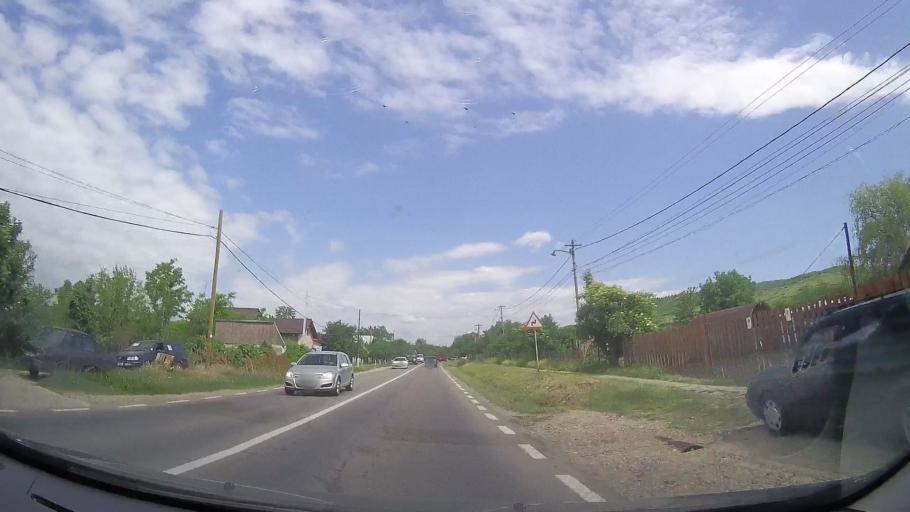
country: RO
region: Prahova
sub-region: Comuna Magurele
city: Magurele
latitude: 45.1096
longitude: 26.0355
